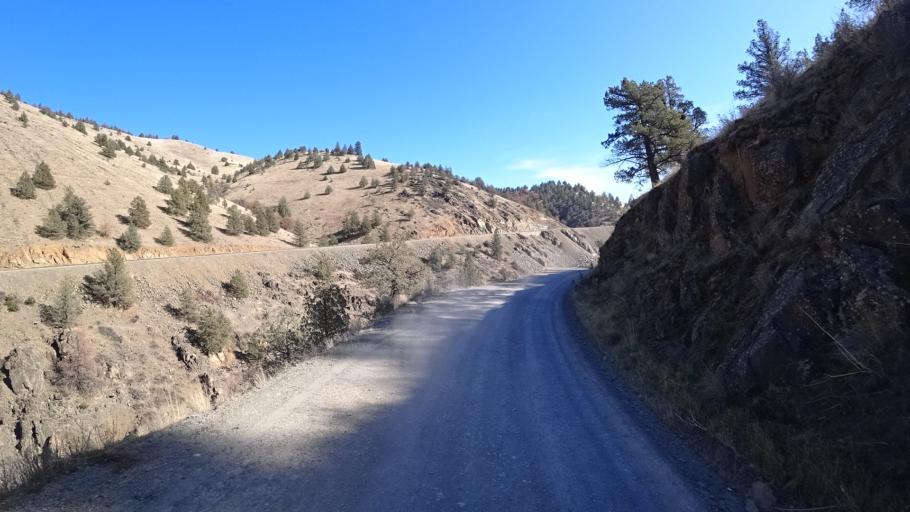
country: US
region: California
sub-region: Siskiyou County
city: Yreka
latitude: 41.7886
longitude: -122.6050
